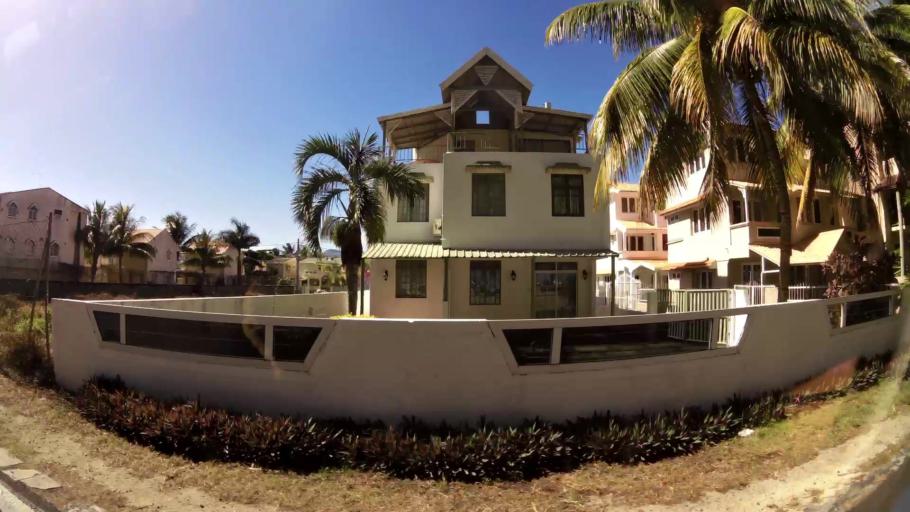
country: MU
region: Black River
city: Flic en Flac
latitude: -20.2894
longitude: 57.3637
